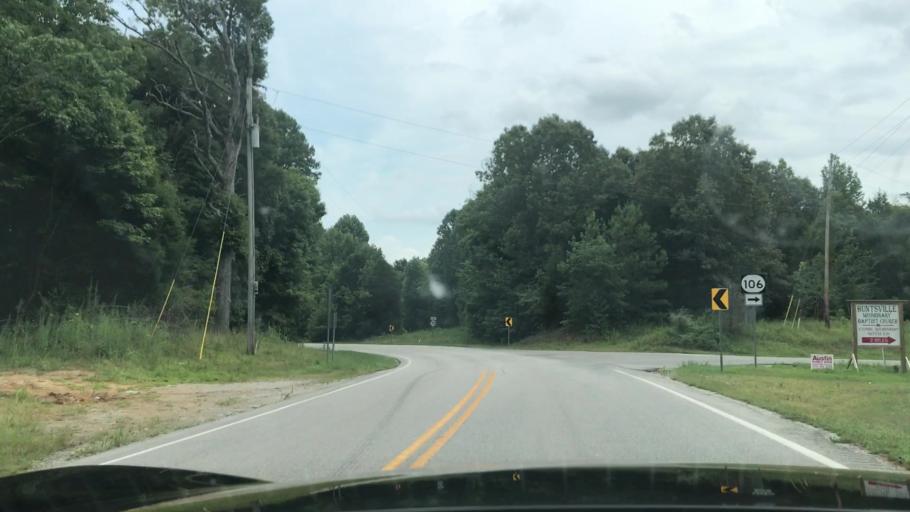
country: US
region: Kentucky
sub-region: Butler County
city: Morgantown
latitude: 37.1853
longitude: -86.8762
